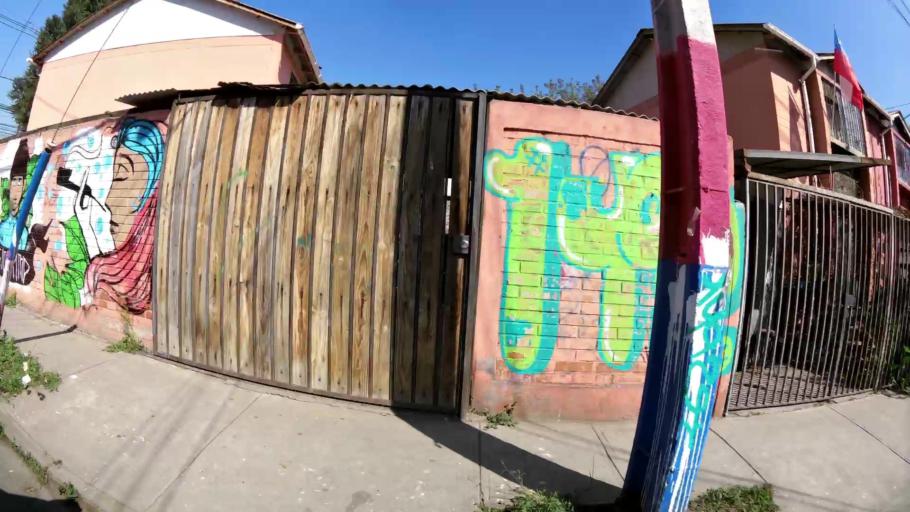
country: CL
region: Santiago Metropolitan
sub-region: Provincia de Santiago
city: Lo Prado
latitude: -33.3573
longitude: -70.7415
